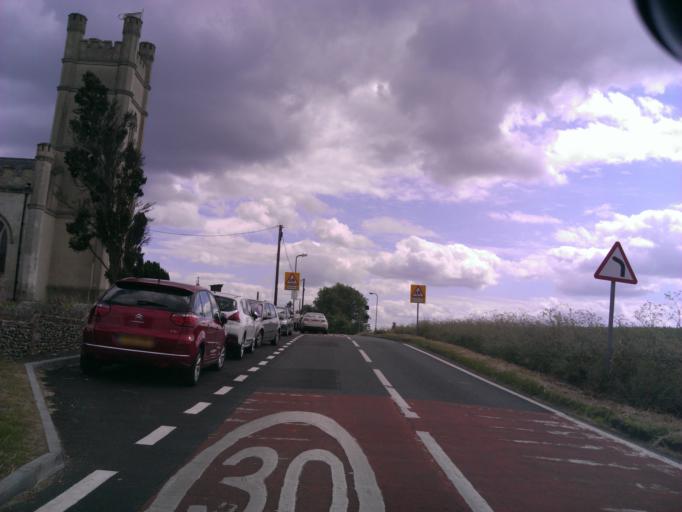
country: GB
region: England
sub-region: Essex
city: Witham
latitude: 51.8292
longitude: 0.6510
